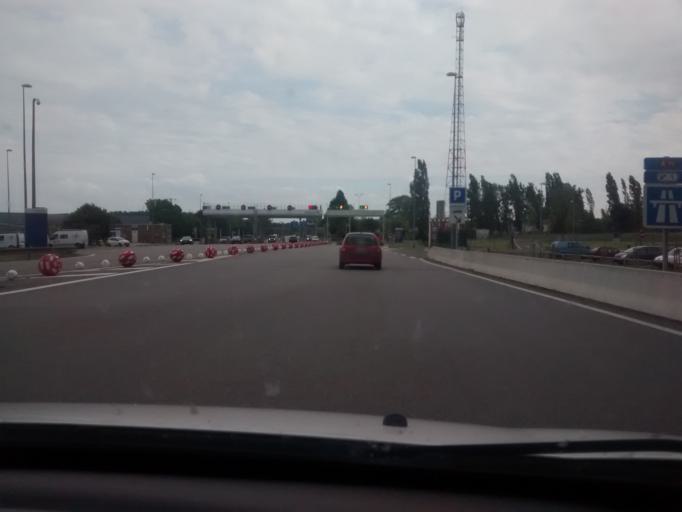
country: FR
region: Ile-de-France
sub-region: Departement des Yvelines
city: Ablis
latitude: 48.5300
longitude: 1.8317
